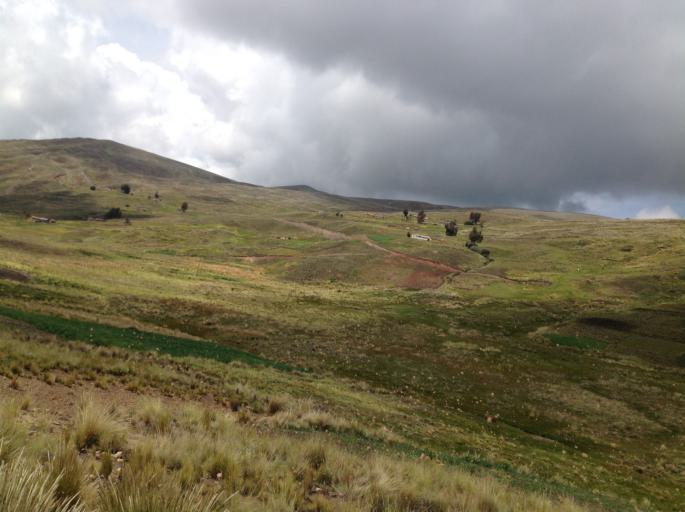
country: BO
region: La Paz
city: Yumani
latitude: -15.7678
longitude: -68.9889
